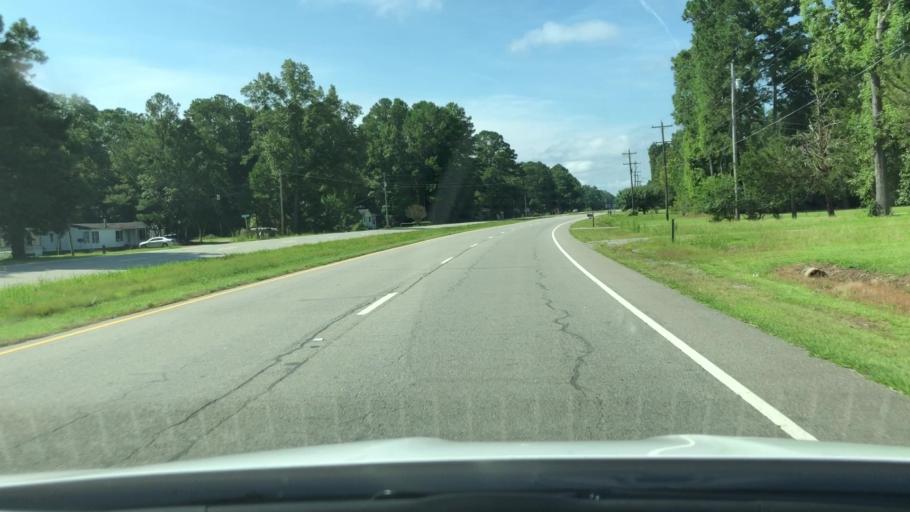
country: US
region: North Carolina
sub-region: Bertie County
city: Windsor
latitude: 35.9615
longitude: -76.9520
